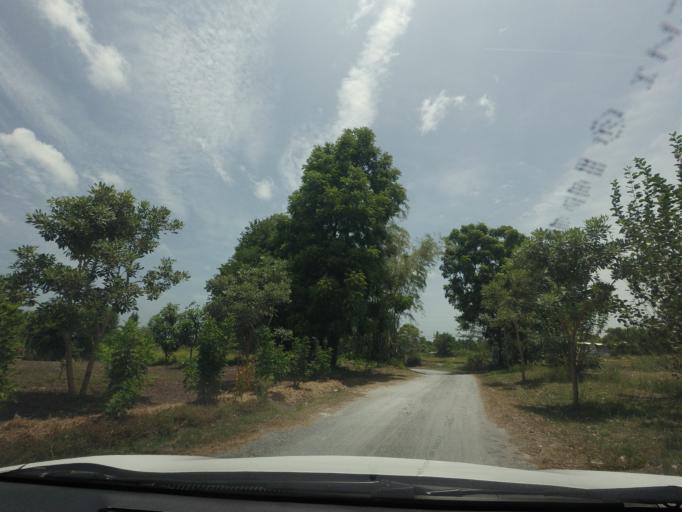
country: TH
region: Chon Buri
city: Chon Buri
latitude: 13.3214
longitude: 100.9794
